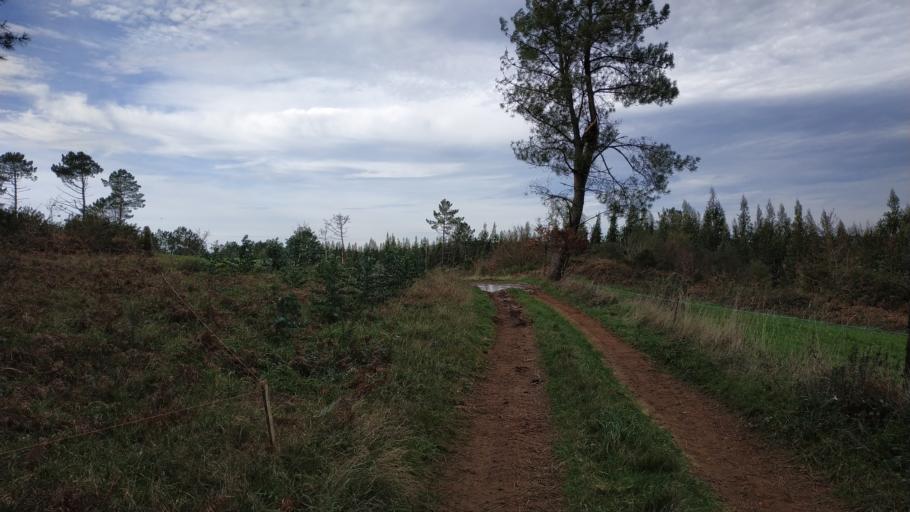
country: ES
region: Galicia
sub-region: Provincia de Pontevedra
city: Silleda
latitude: 42.7735
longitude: -8.1627
